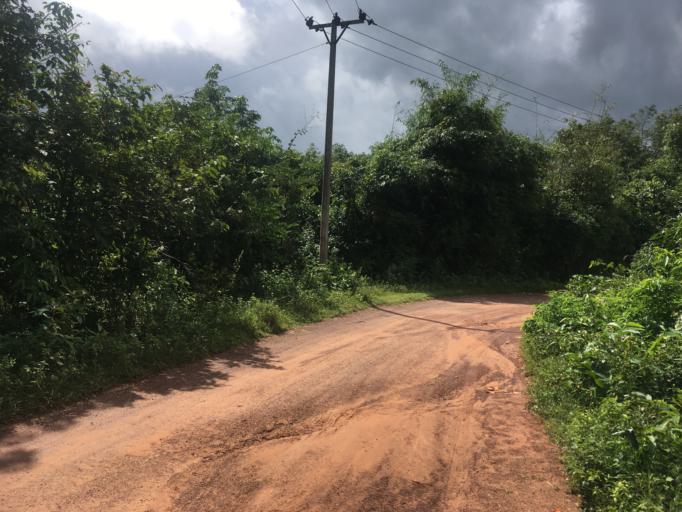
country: MM
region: Mon
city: Mawlamyine
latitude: 16.4602
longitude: 97.6895
